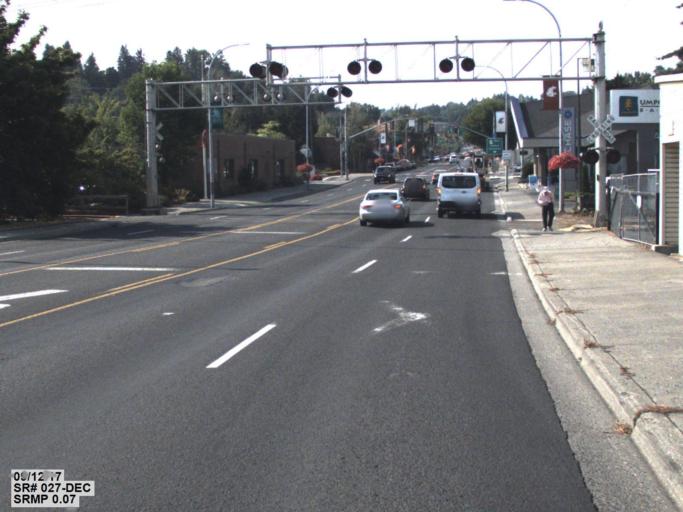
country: US
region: Washington
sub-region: Whitman County
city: Pullman
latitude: 46.7316
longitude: -117.1801
